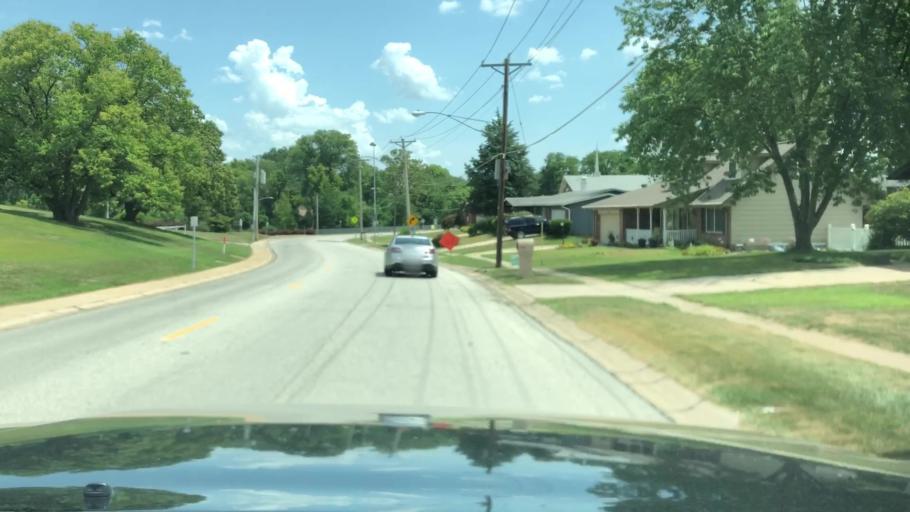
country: US
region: Missouri
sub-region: Saint Charles County
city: Saint Charles
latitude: 38.7983
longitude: -90.5273
